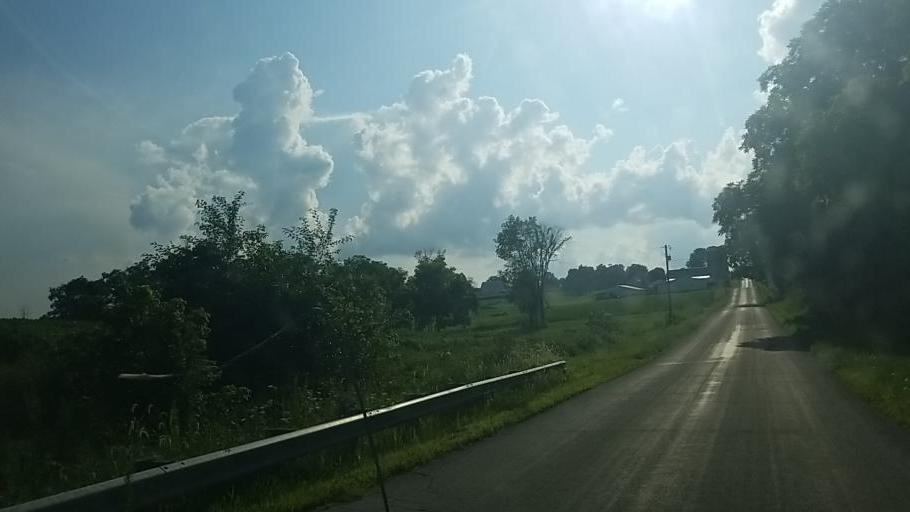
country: US
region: Ohio
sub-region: Wayne County
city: West Salem
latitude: 40.9009
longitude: -82.0454
